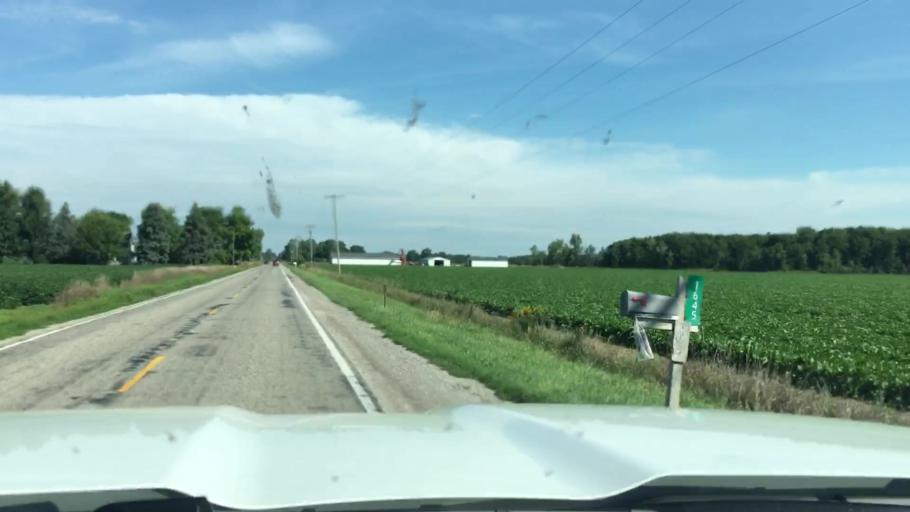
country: US
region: Michigan
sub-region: Saginaw County
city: Hemlock
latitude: 43.4311
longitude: -84.2299
